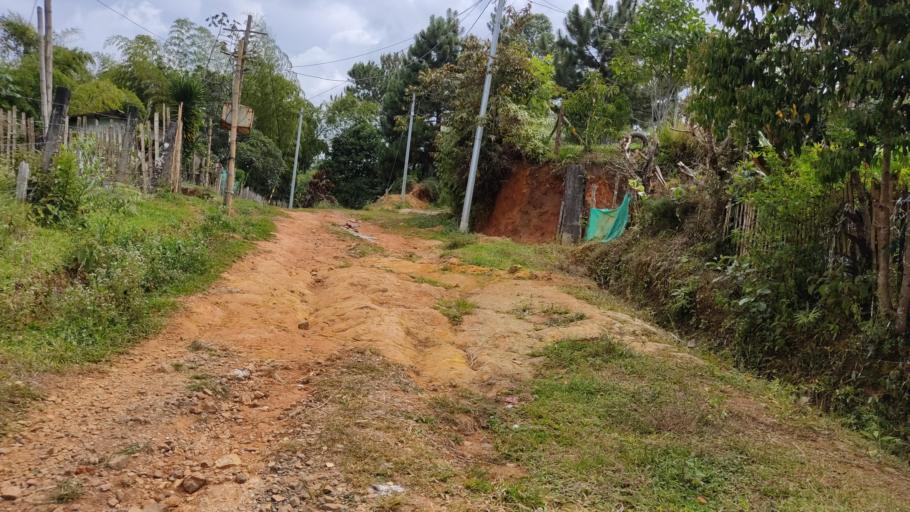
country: CO
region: Valle del Cauca
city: Jamundi
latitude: 3.2110
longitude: -76.6566
